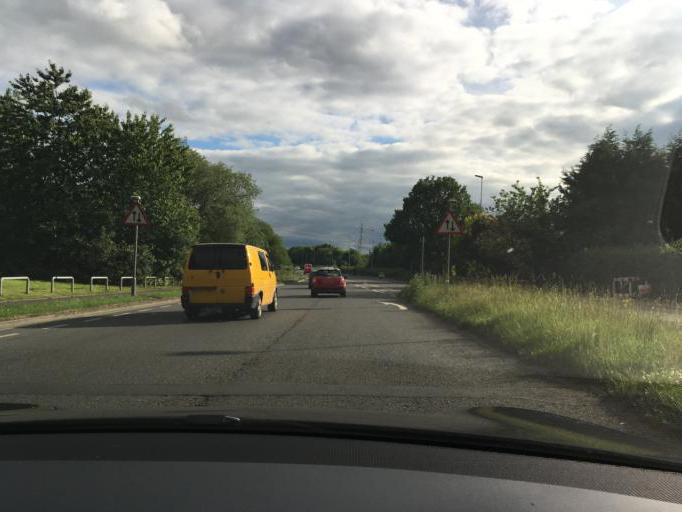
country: GB
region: England
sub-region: Trafford
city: Carrington
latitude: 53.4634
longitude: -2.3972
